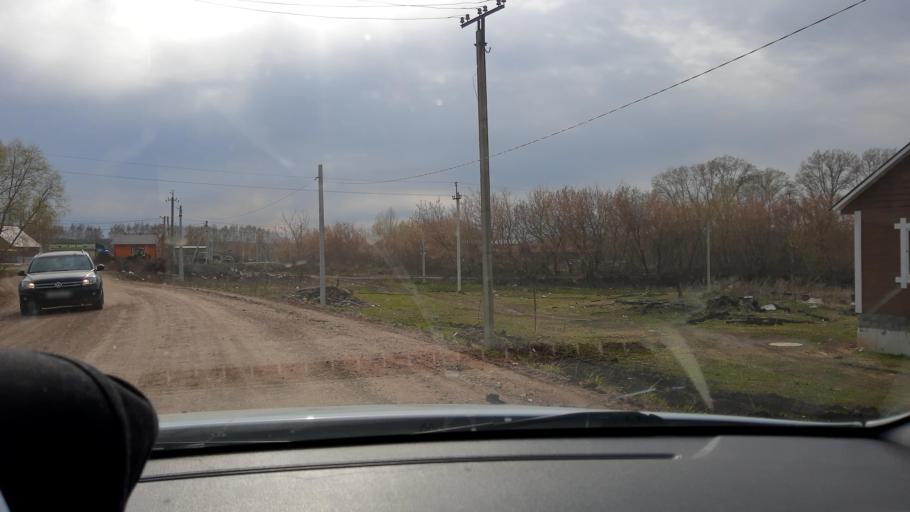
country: RU
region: Bashkortostan
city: Iglino
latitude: 54.8065
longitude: 56.4275
